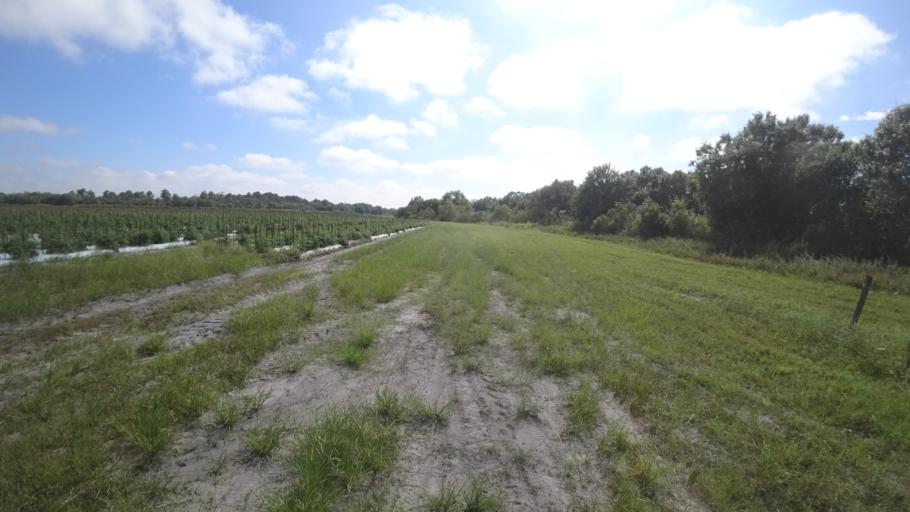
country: US
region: Florida
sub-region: DeSoto County
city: Arcadia
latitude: 27.2789
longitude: -82.0812
